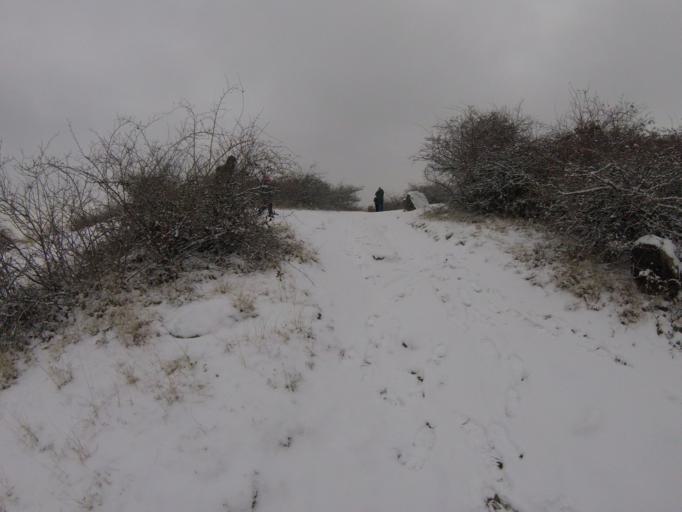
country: HU
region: Fejer
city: Pakozd
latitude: 47.2355
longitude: 18.5380
